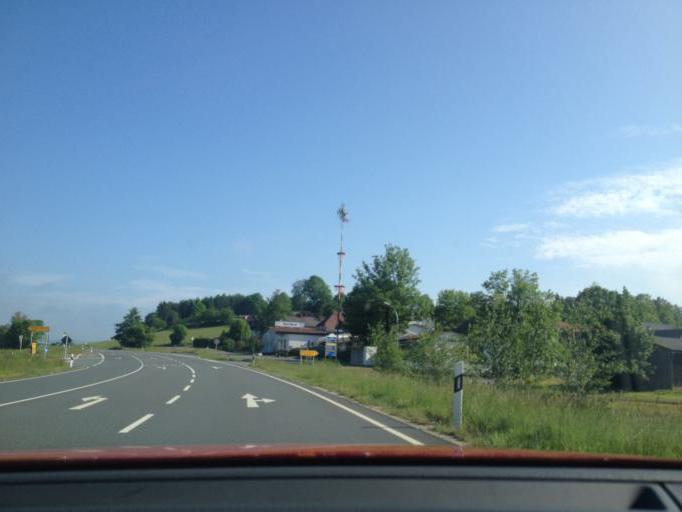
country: DE
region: Bavaria
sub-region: Upper Palatinate
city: Kastl
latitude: 49.8439
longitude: 11.8898
